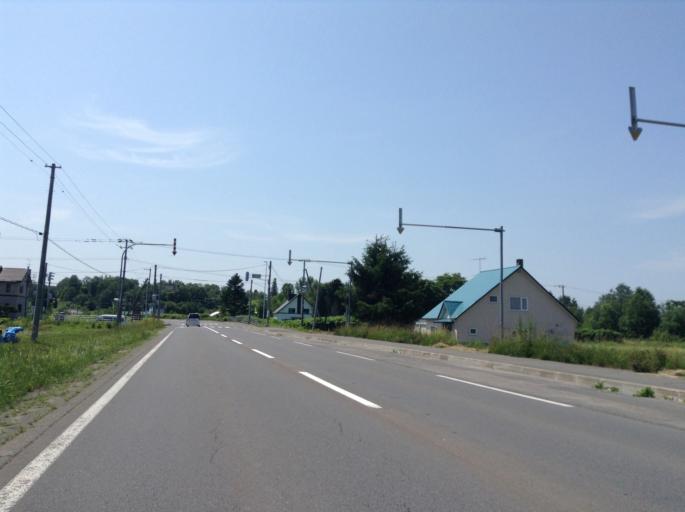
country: JP
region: Hokkaido
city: Nayoro
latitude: 44.3524
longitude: 142.4733
